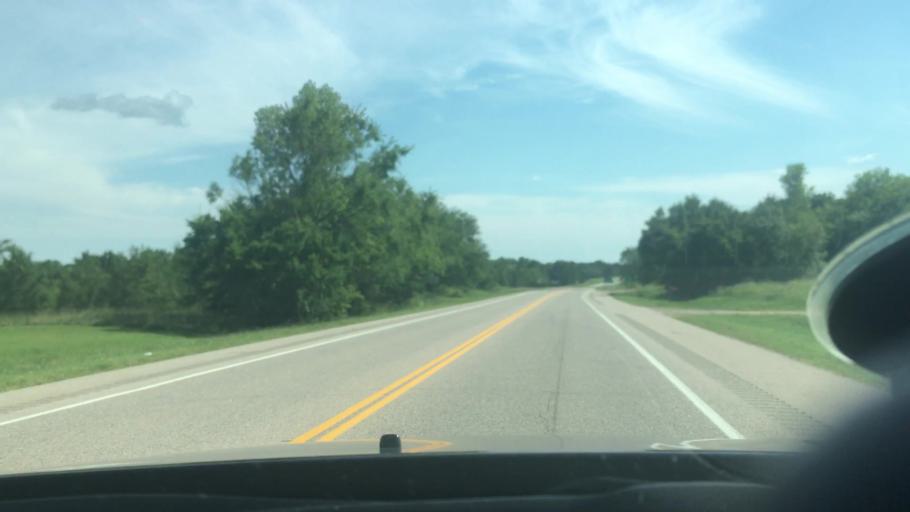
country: US
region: Oklahoma
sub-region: Seminole County
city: Seminole
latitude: 35.1523
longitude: -96.6748
